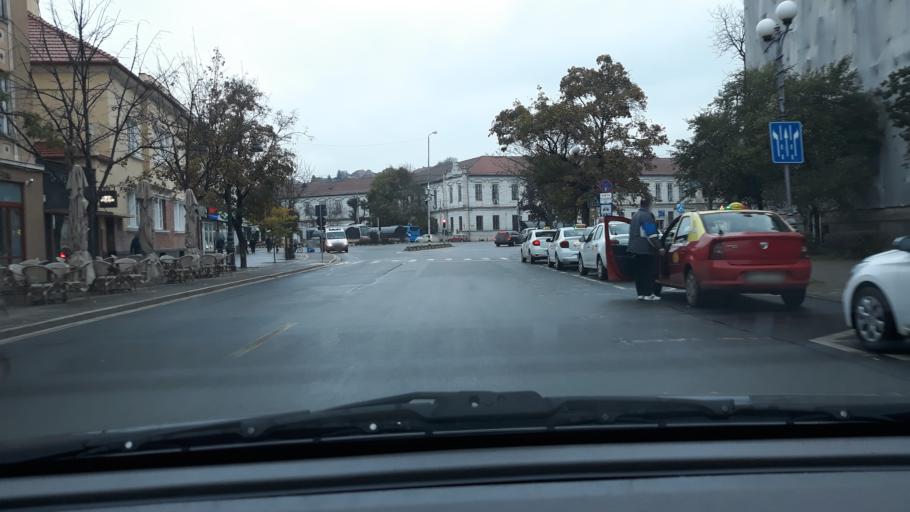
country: RO
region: Bihor
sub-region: Comuna Biharea
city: Oradea
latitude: 47.0610
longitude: 21.9379
